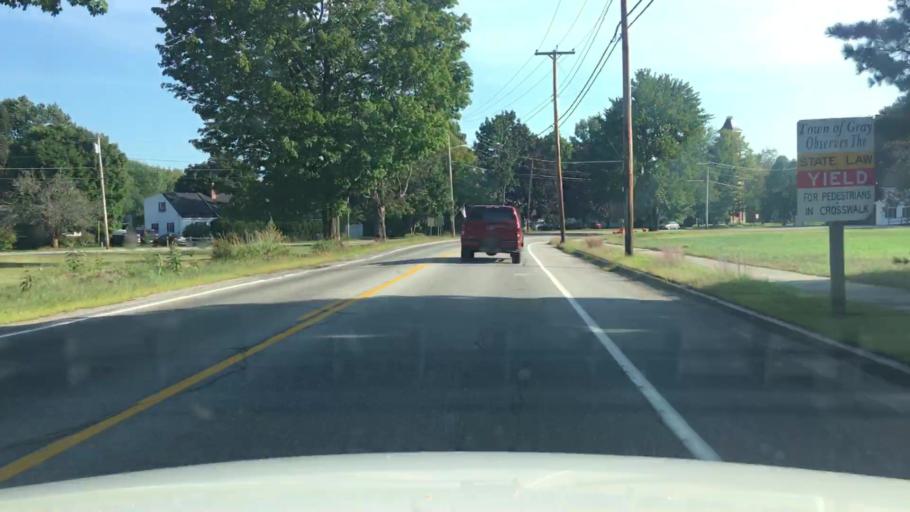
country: US
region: Maine
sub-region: Cumberland County
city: New Gloucester
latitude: 43.8900
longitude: -70.3276
